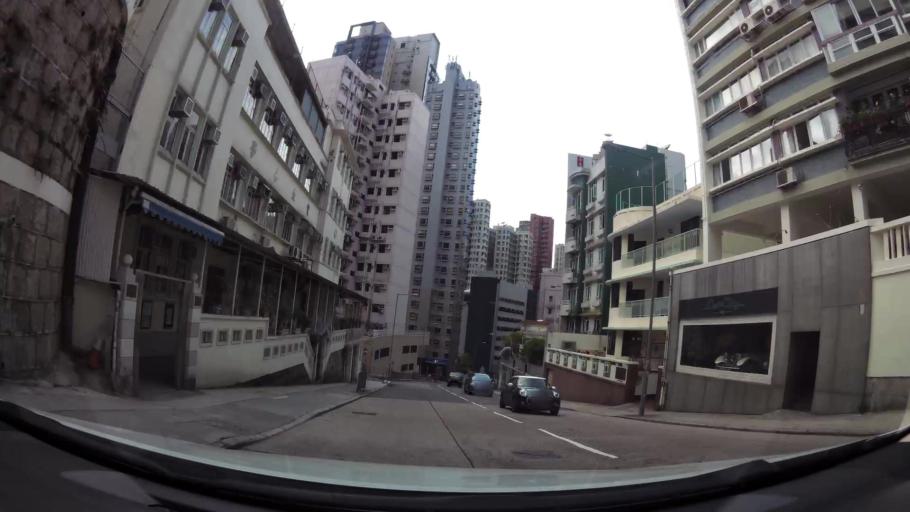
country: HK
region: Wanchai
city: Wan Chai
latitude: 22.2664
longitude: 114.1882
